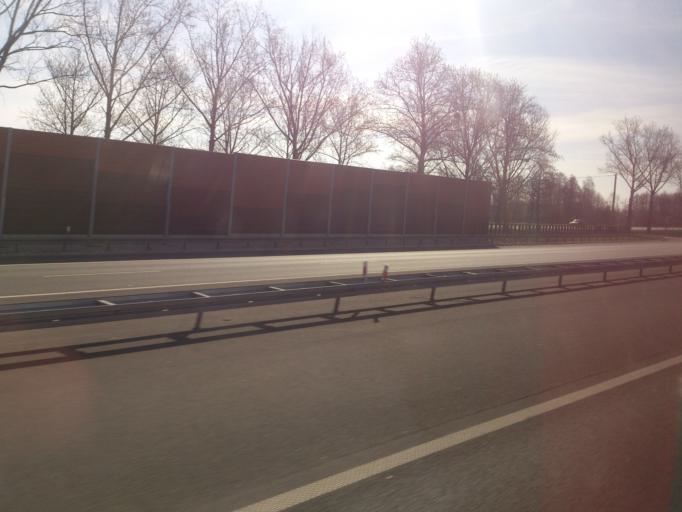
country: PL
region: Kujawsko-Pomorskie
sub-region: Powiat aleksandrowski
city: Raciazek
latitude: 52.8067
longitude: 18.8165
